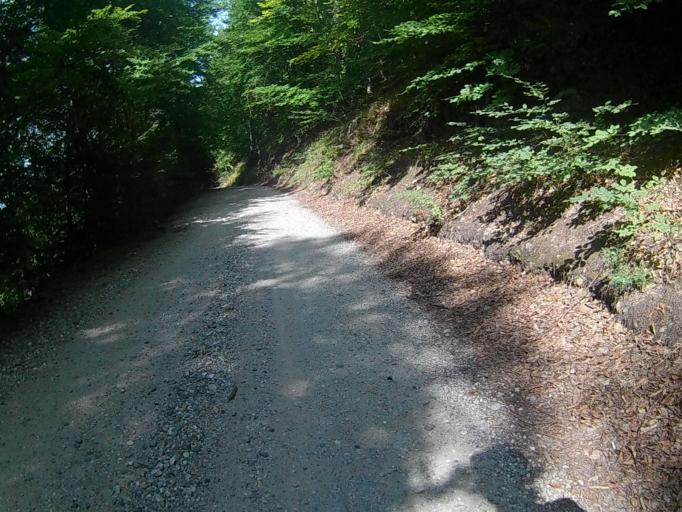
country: SI
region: Ruse
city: Bistrica ob Dravi
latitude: 46.5193
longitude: 15.5651
